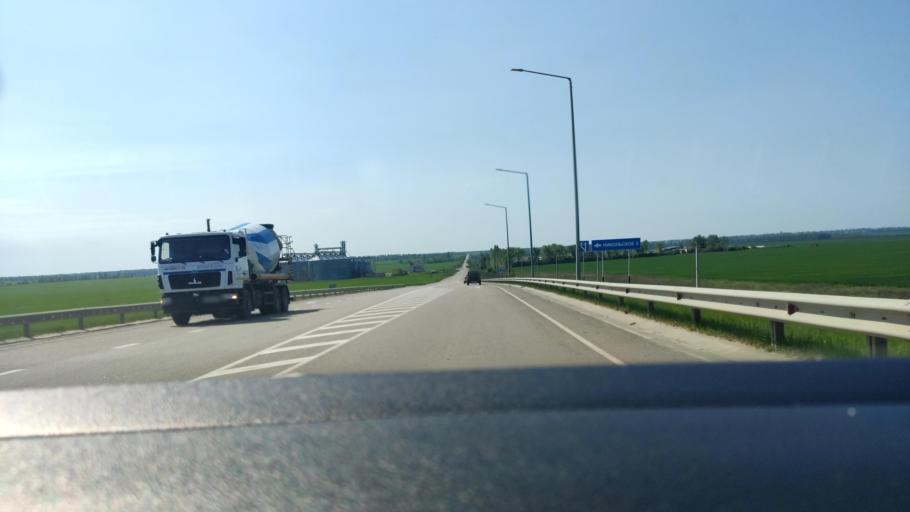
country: RU
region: Voronezj
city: Novaya Usman'
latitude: 51.5884
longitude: 39.3740
